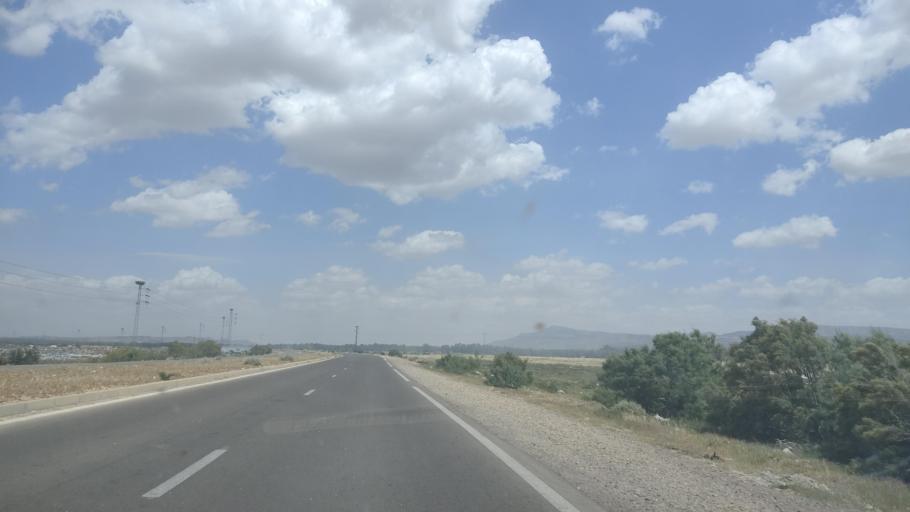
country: TN
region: Al Qasrayn
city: Kasserine
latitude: 35.1982
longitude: 8.8478
